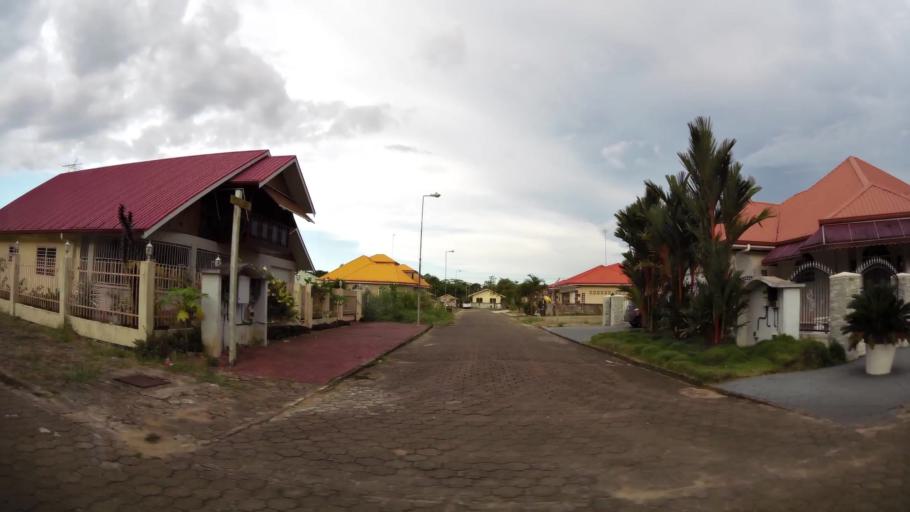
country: SR
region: Paramaribo
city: Paramaribo
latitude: 5.8628
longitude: -55.1769
